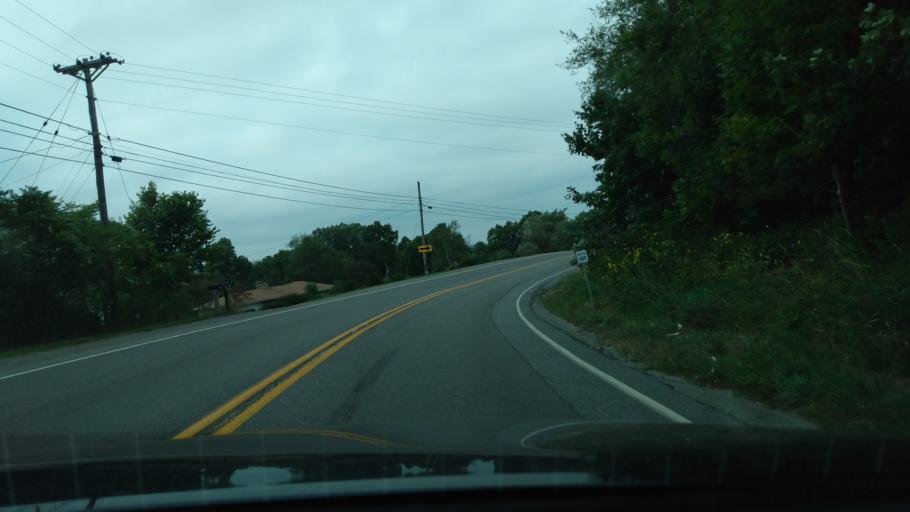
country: US
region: Pennsylvania
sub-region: Cambria County
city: Hastings
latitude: 40.6178
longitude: -78.7153
